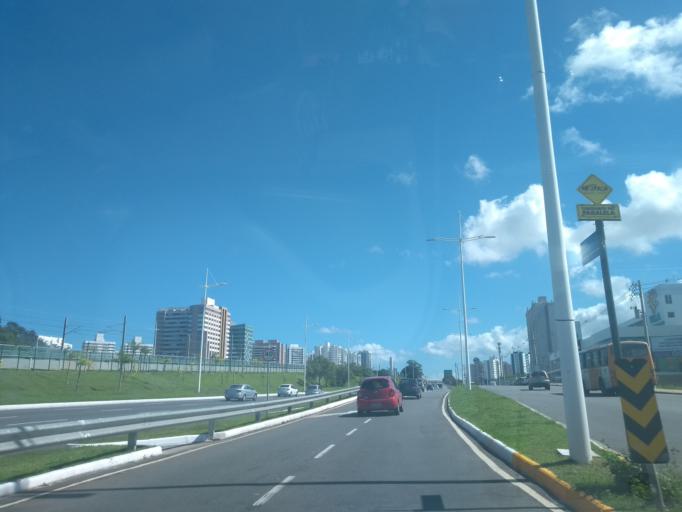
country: BR
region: Bahia
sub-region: Lauro De Freitas
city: Lauro de Freitas
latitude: -12.9366
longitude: -38.3998
